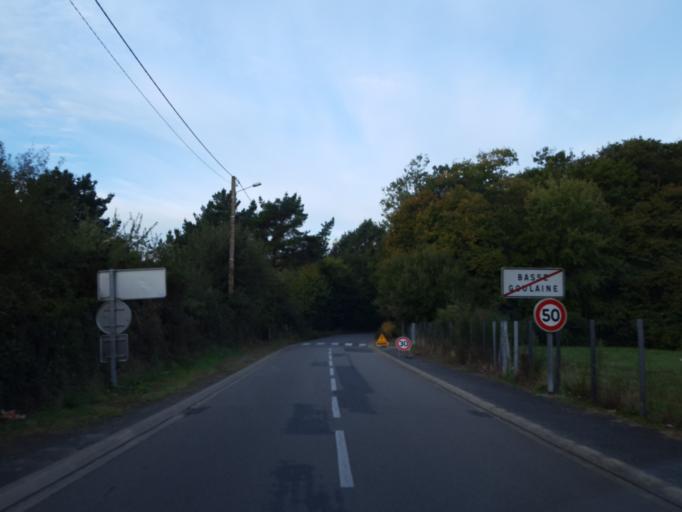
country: FR
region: Pays de la Loire
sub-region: Departement de la Loire-Atlantique
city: Basse-Goulaine
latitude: 47.2004
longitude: -1.4753
